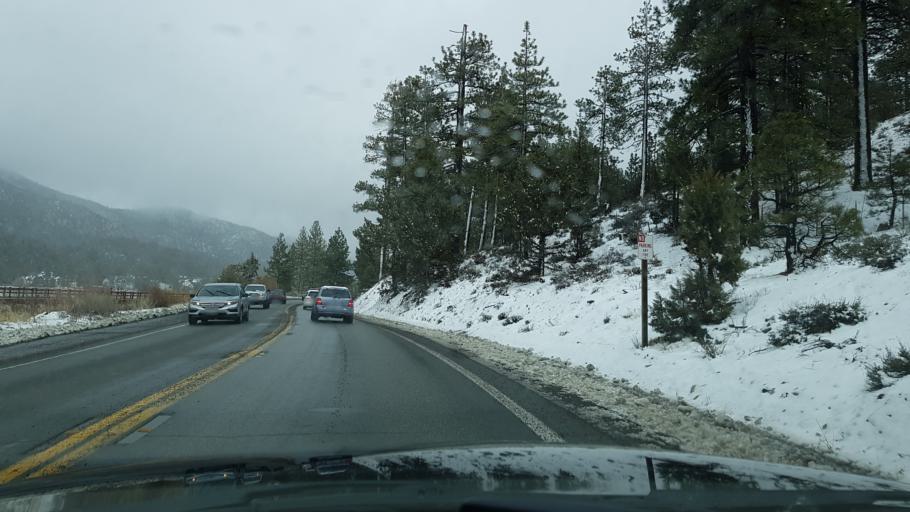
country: US
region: California
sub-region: San Bernardino County
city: Big Bear Lake
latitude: 34.2585
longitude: -116.8804
